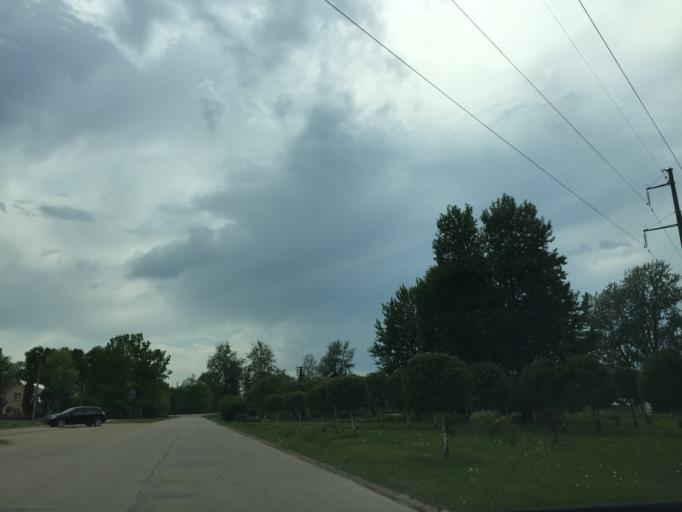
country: LV
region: Livani
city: Livani
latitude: 56.5368
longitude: 26.2414
